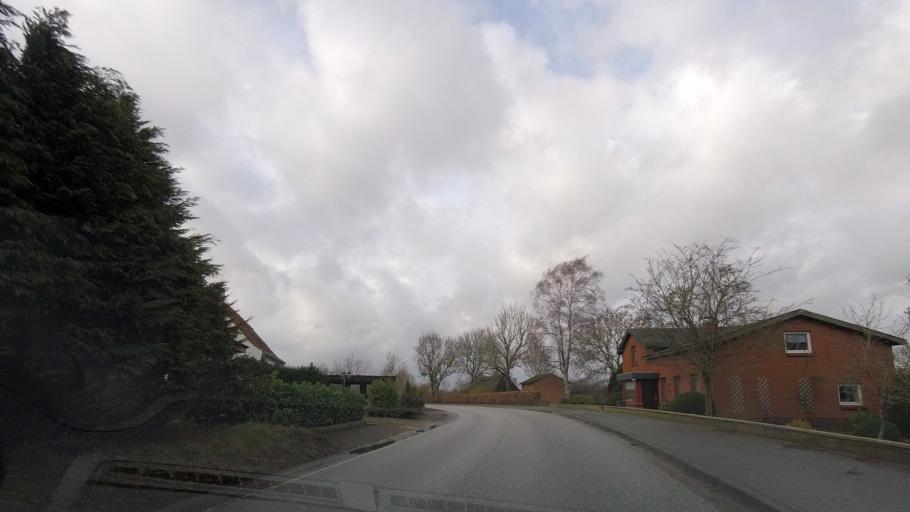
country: DE
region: Schleswig-Holstein
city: Dollrottfeld
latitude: 54.6429
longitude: 9.8128
